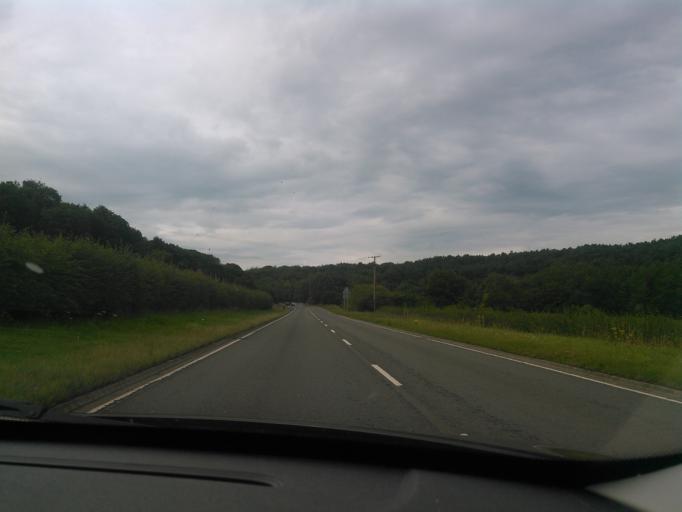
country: GB
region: England
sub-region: Shropshire
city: Prees
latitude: 52.8425
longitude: -2.6621
